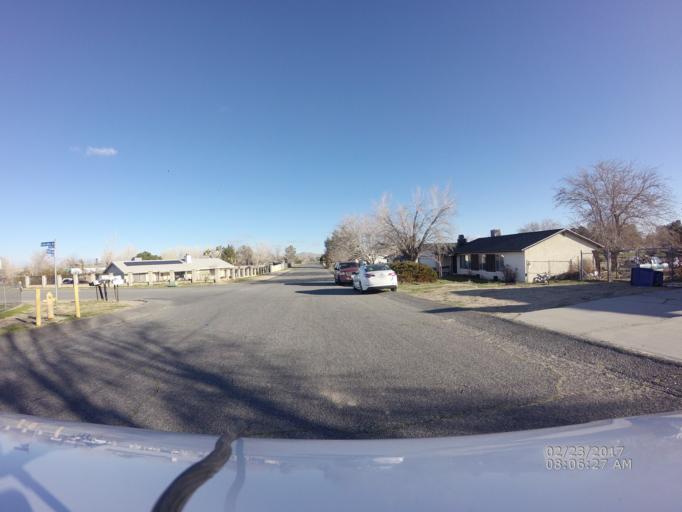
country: US
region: California
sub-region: Los Angeles County
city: Lake Los Angeles
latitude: 34.6128
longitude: -117.8208
